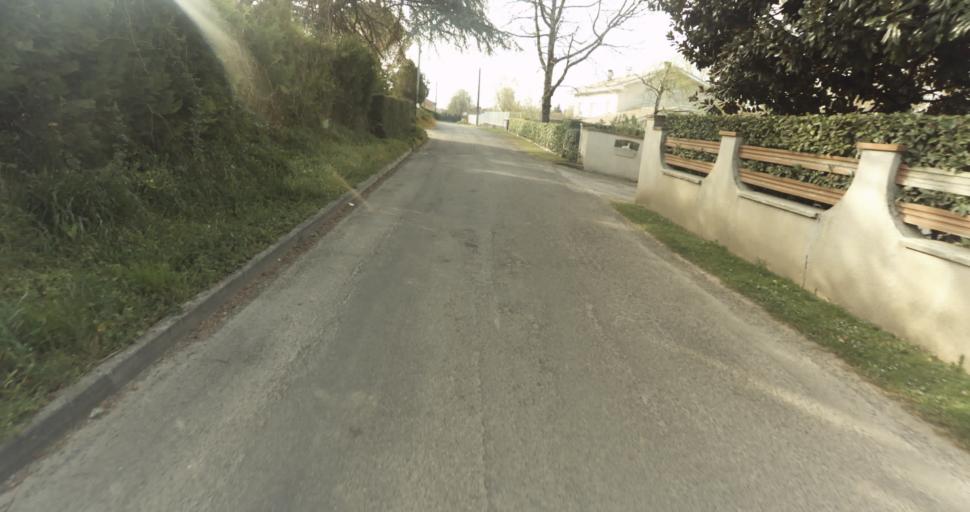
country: FR
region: Midi-Pyrenees
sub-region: Departement du Tarn-et-Garonne
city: Moissac
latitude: 44.1188
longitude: 1.1078
